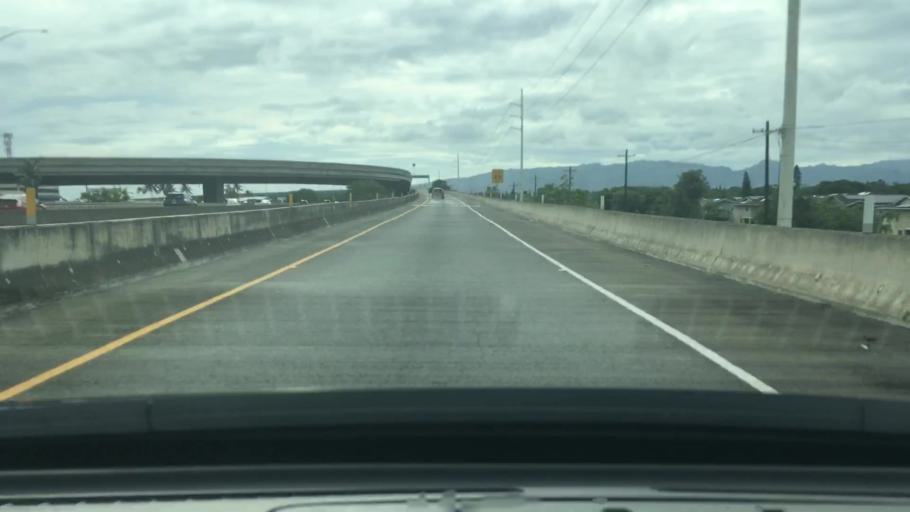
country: US
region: Hawaii
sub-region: Honolulu County
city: Halawa Heights
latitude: 21.3373
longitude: -157.9130
